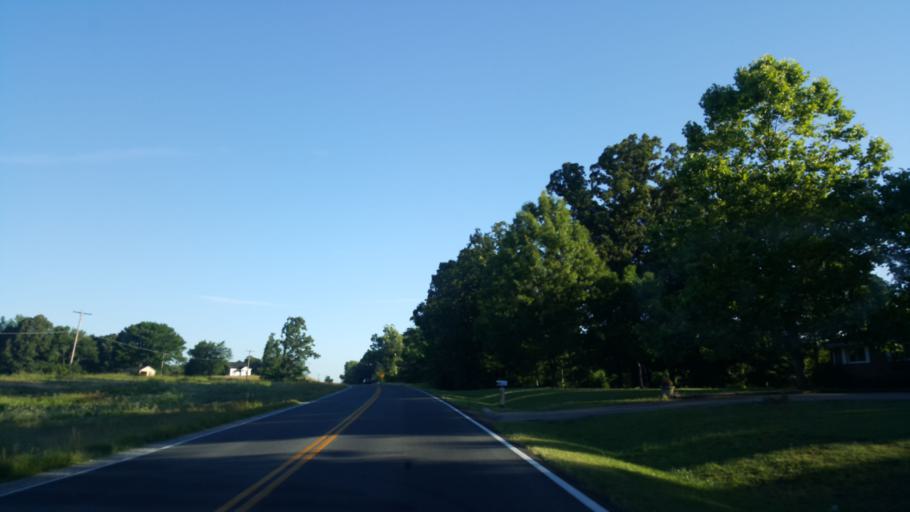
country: US
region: Tennessee
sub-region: Henderson County
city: Lexington
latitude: 35.5993
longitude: -88.3902
